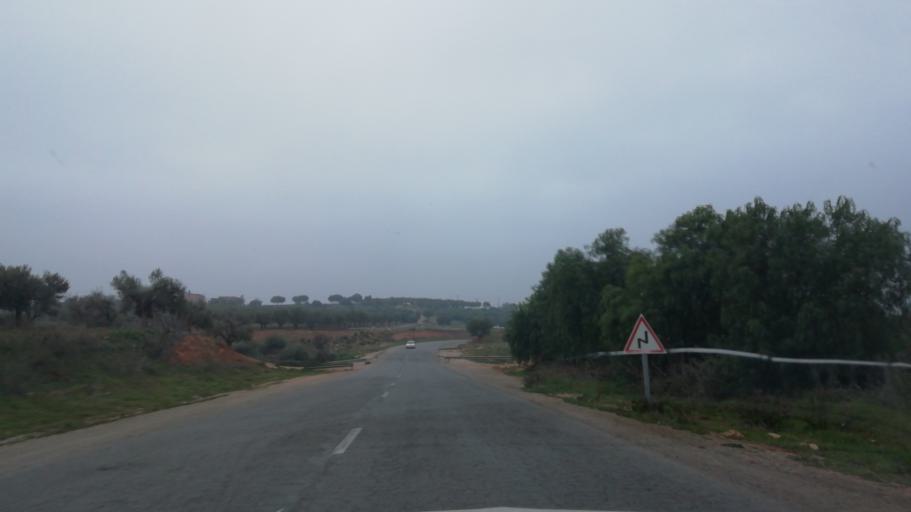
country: DZ
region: Mascara
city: Mascara
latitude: 35.3888
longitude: 0.1617
